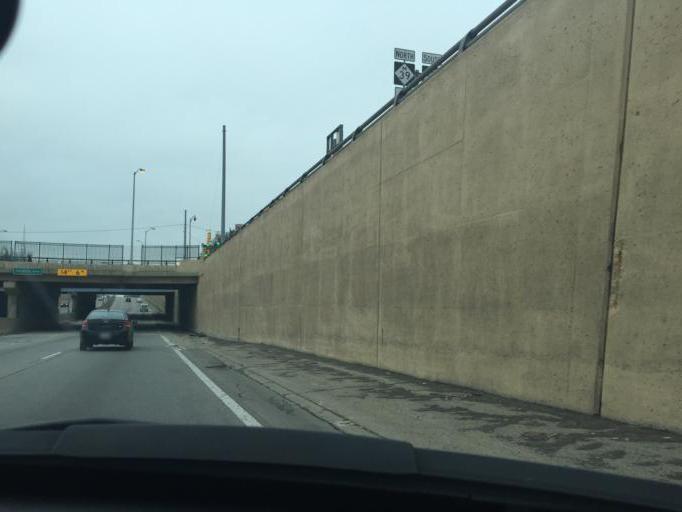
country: US
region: Michigan
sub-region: Oakland County
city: Oak Park
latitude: 42.4019
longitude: -83.2185
